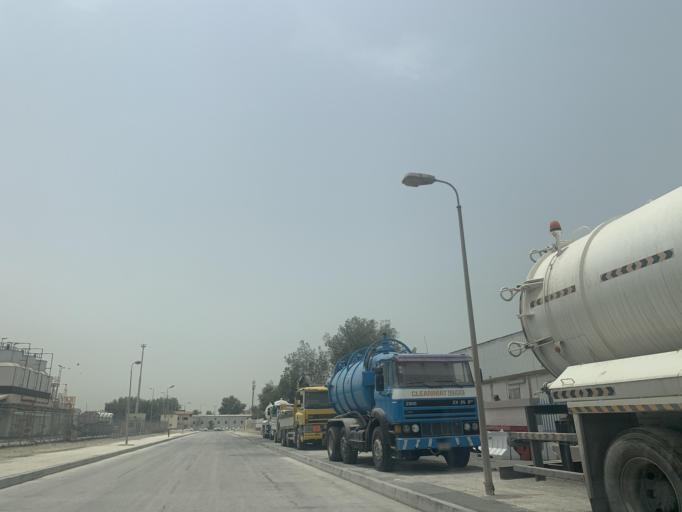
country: BH
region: Northern
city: Sitrah
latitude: 26.1795
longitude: 50.6124
